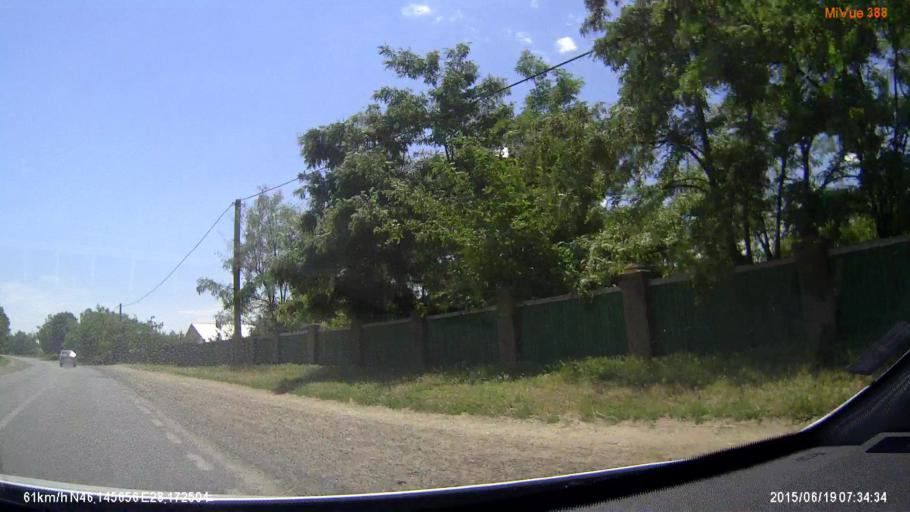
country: RO
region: Vaslui
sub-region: Oras Murgeni
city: Carja
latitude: 46.1461
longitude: 28.1726
